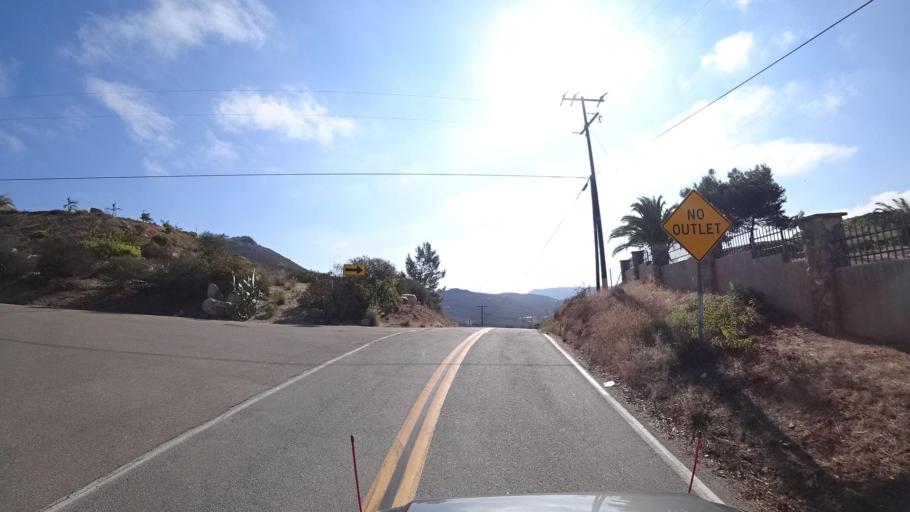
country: US
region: California
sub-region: San Diego County
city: Lake San Marcos
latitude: 33.0971
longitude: -117.1748
